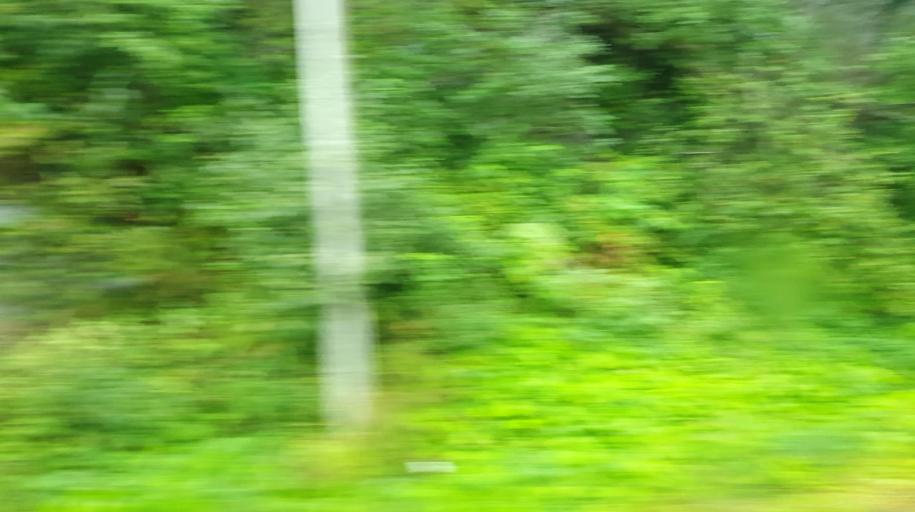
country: NO
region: Sor-Trondelag
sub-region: Melhus
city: Melhus
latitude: 63.3215
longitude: 10.2016
